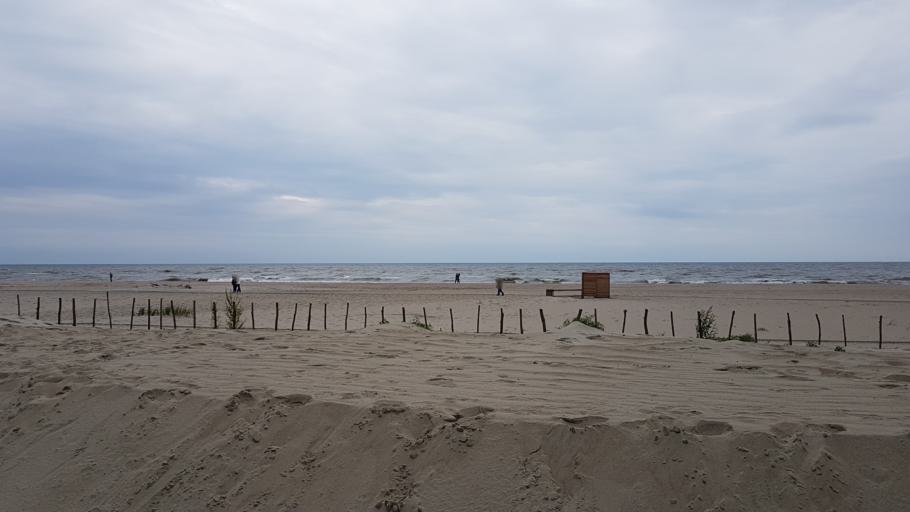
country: RU
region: Kaliningrad
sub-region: Gorod Kaliningrad
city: Yantarnyy
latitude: 54.8706
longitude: 19.9336
